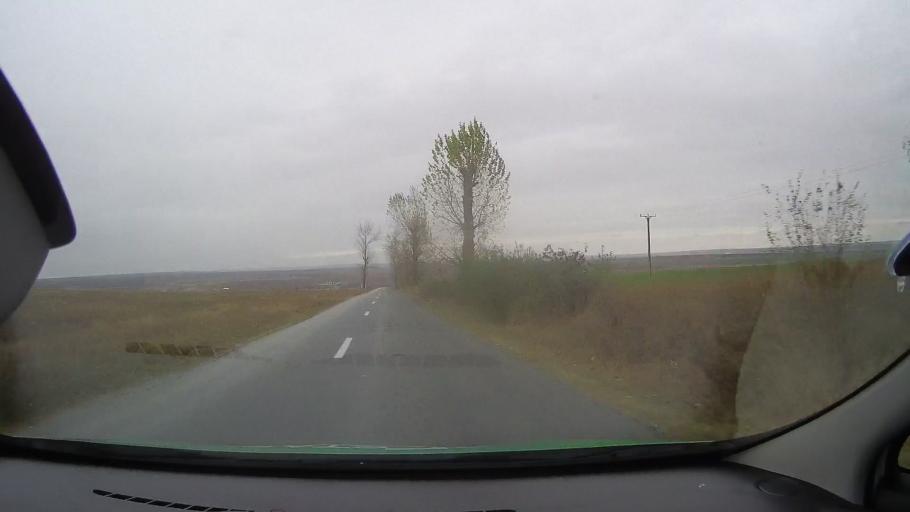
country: RO
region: Constanta
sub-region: Comuna Pantelimon
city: Pantelimon
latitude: 44.5861
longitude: 28.3144
